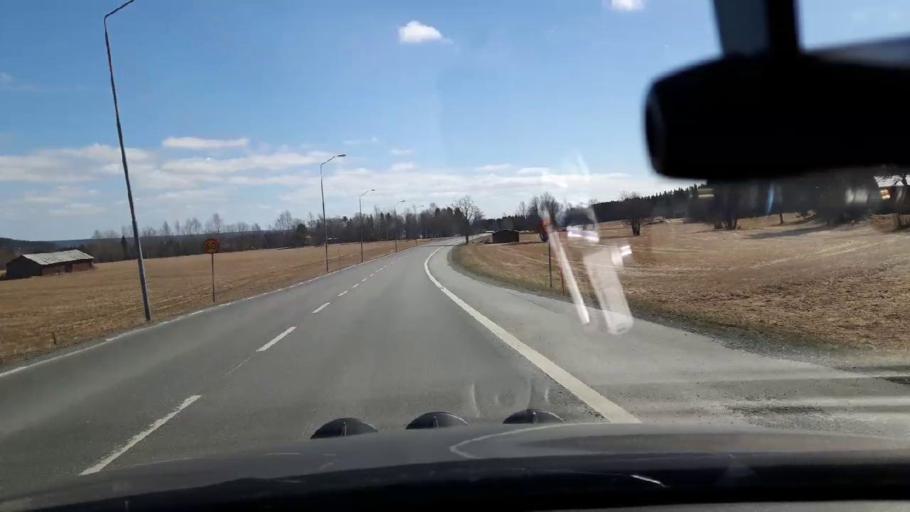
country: SE
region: Jaemtland
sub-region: OEstersunds Kommun
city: Ostersund
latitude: 63.1784
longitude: 14.5221
